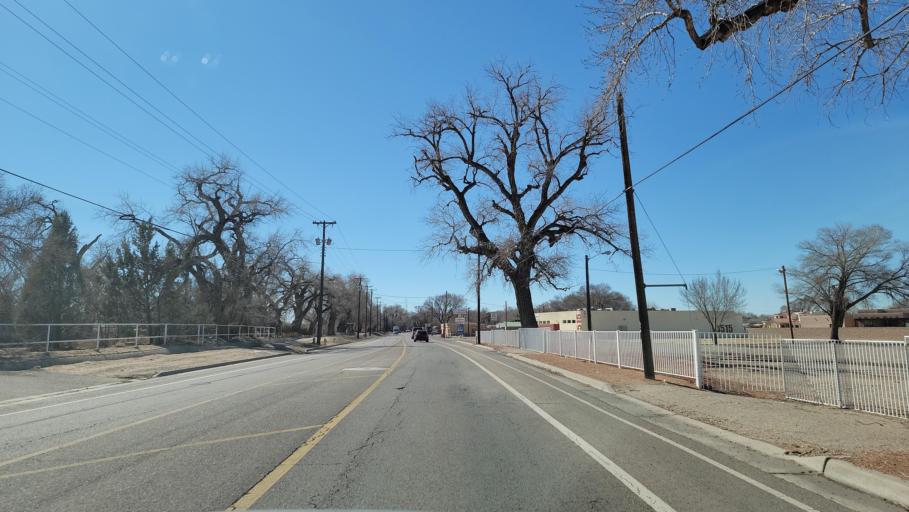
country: US
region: New Mexico
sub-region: Bernalillo County
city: South Valley
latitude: 35.0109
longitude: -106.6876
